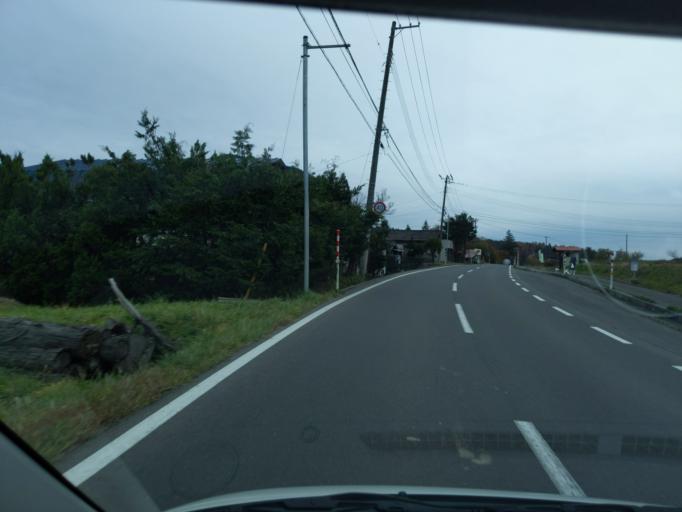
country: JP
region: Iwate
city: Kitakami
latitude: 39.2744
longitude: 141.2676
